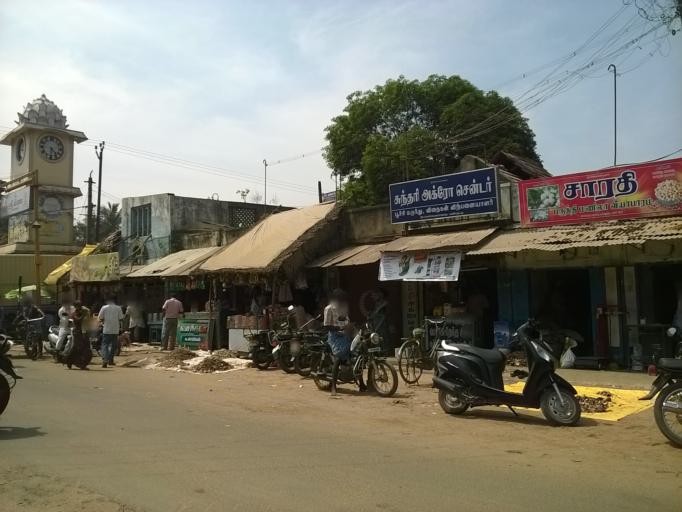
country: IN
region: Tamil Nadu
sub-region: Cuddalore
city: Panruti
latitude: 11.7731
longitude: 79.5518
